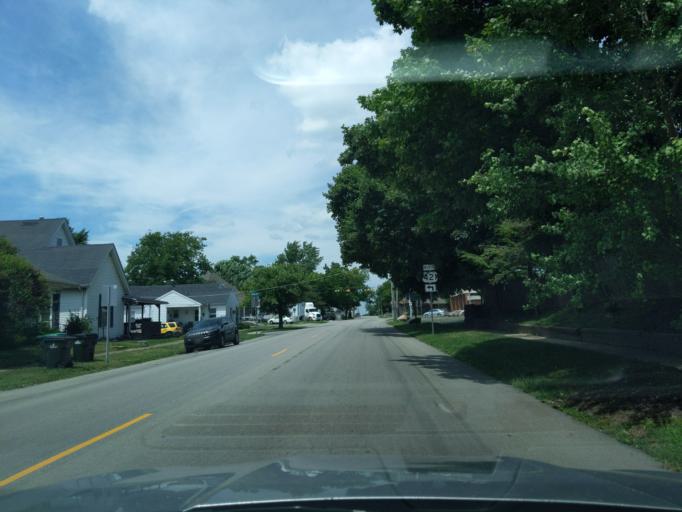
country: US
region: Indiana
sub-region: Decatur County
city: Greensburg
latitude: 39.3406
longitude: -85.4889
